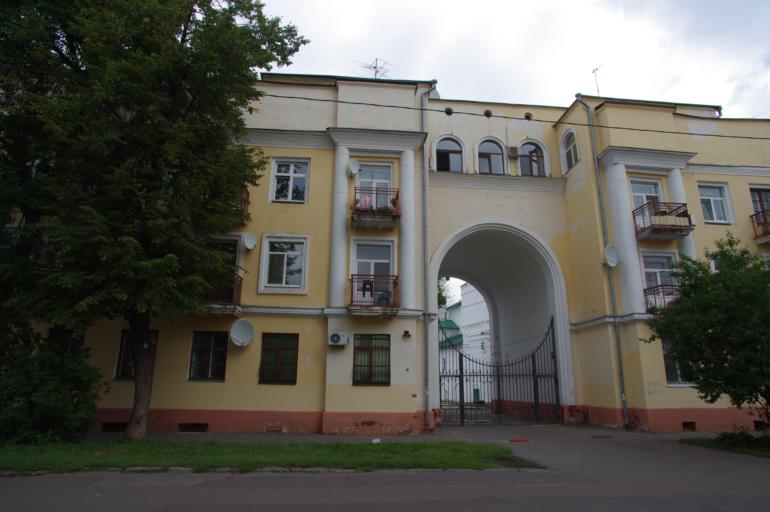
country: RU
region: Jaroslavl
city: Yaroslavl
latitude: 57.6288
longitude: 39.8947
